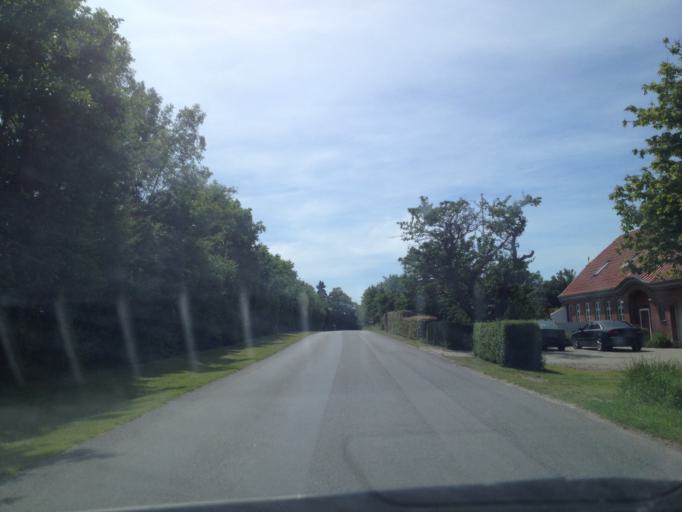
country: DK
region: Central Jutland
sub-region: Samso Kommune
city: Tranebjerg
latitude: 55.8409
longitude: 10.6159
